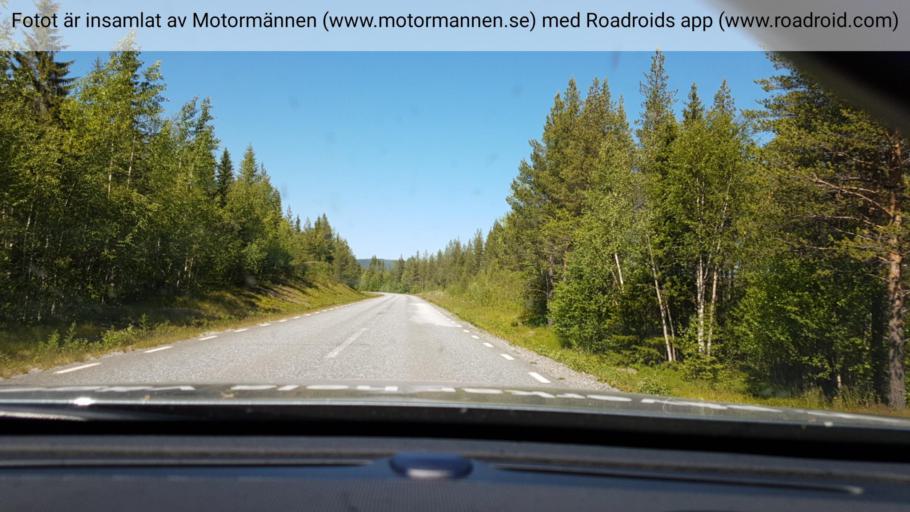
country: SE
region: Vaesterbotten
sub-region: Vilhelmina Kommun
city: Sjoberg
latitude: 64.8666
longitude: 15.8957
